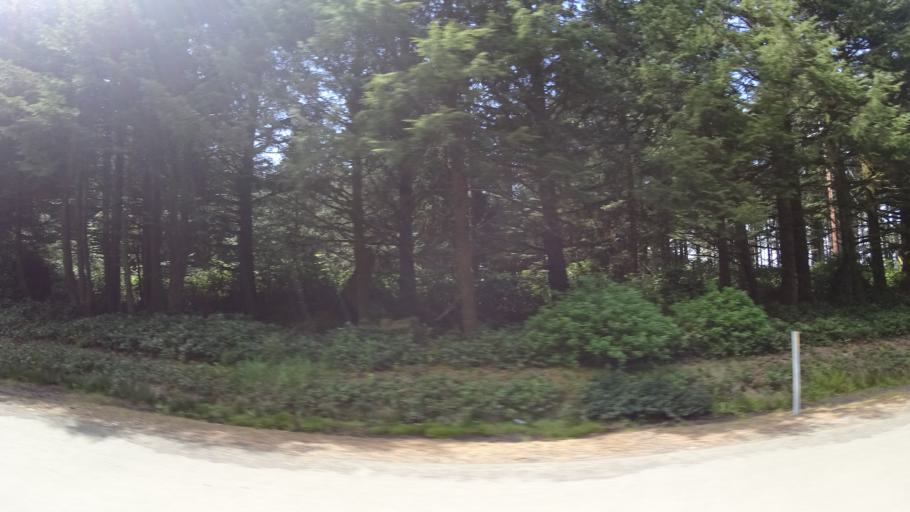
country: US
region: Oregon
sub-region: Lincoln County
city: Lincoln Beach
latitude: 44.8370
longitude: -124.0526
